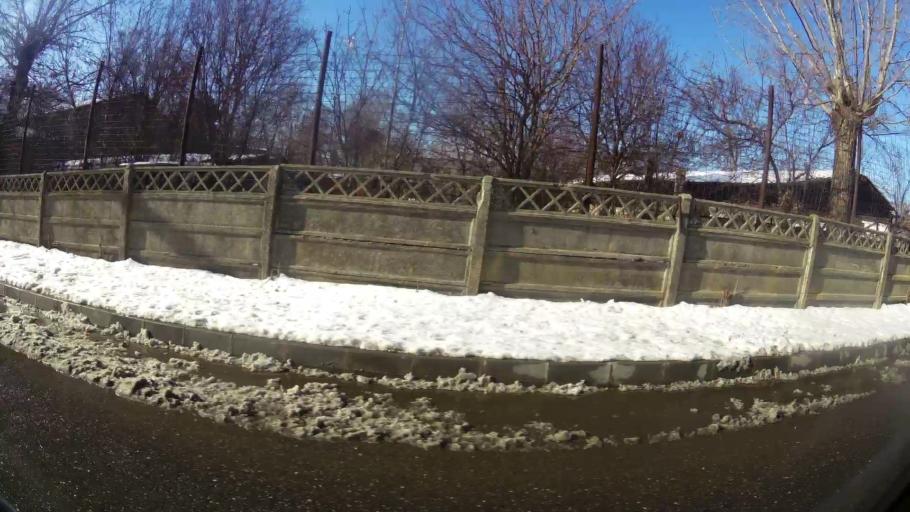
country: RO
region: Ilfov
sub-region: Comuna Magurele
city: Magurele
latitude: 44.3894
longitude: 26.0534
